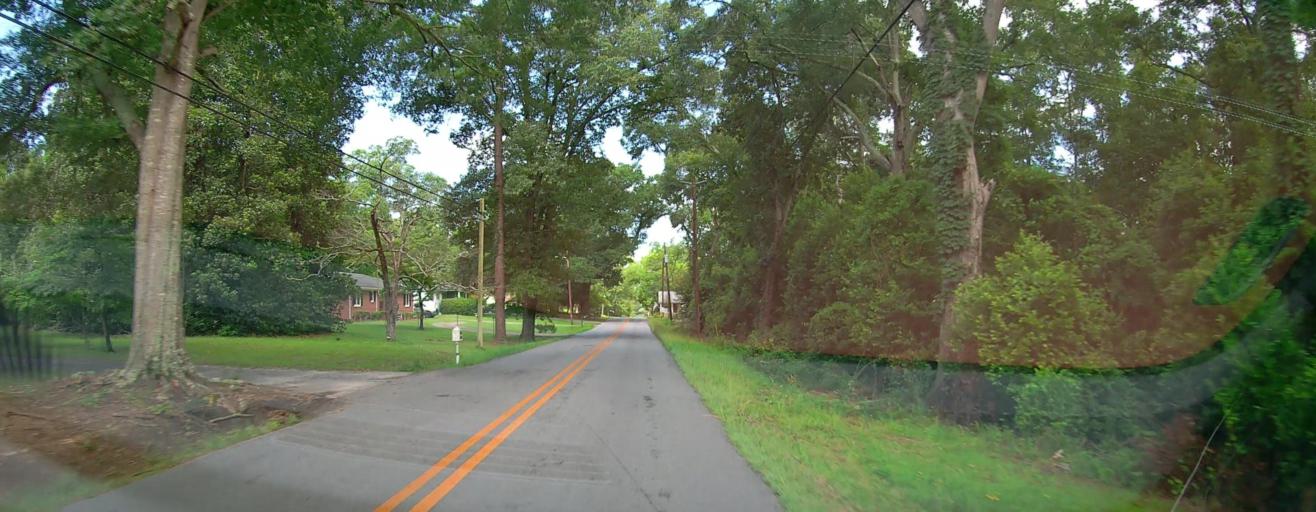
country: US
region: Georgia
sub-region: Peach County
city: Byron
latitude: 32.6550
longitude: -83.7622
